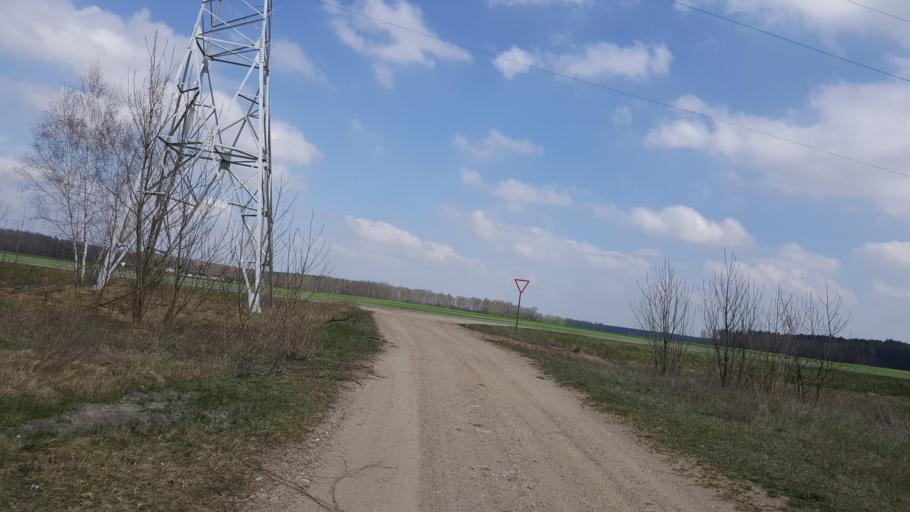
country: BY
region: Brest
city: Zhabinka
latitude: 52.2525
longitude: 23.9677
